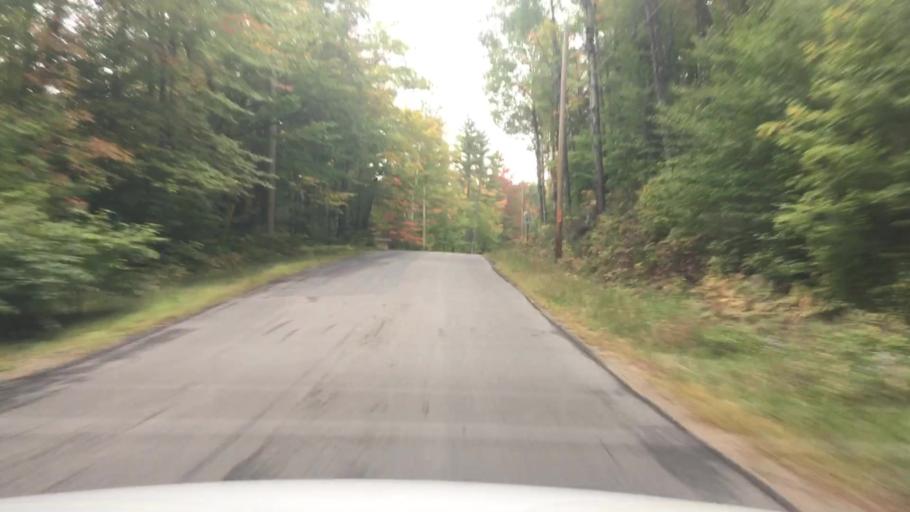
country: US
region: Maine
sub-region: Oxford County
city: Bethel
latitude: 44.4733
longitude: -70.7837
